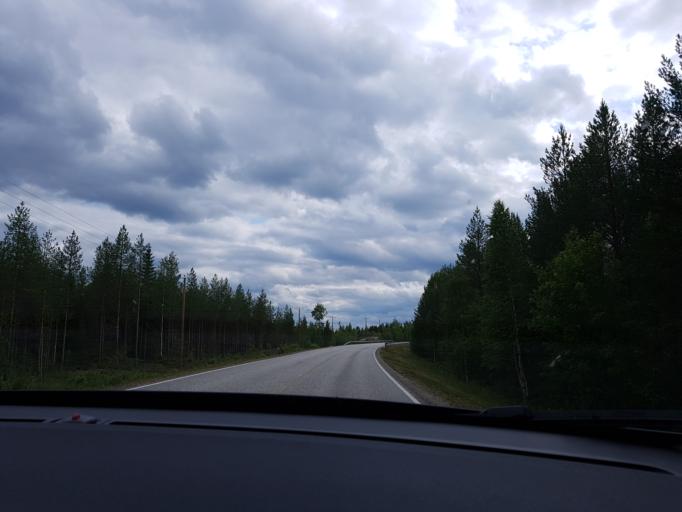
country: FI
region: Kainuu
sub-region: Kehys-Kainuu
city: Kuhmo
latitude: 64.2339
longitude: 29.8191
